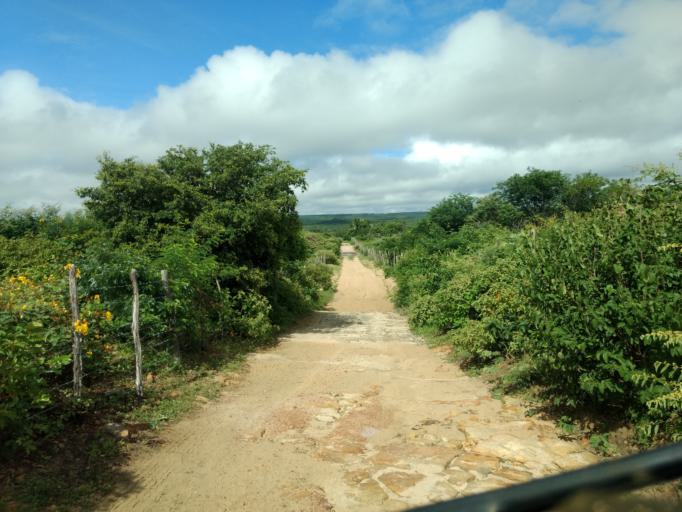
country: BR
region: Ceara
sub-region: Crateus
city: Crateus
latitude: -5.1980
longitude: -40.9532
